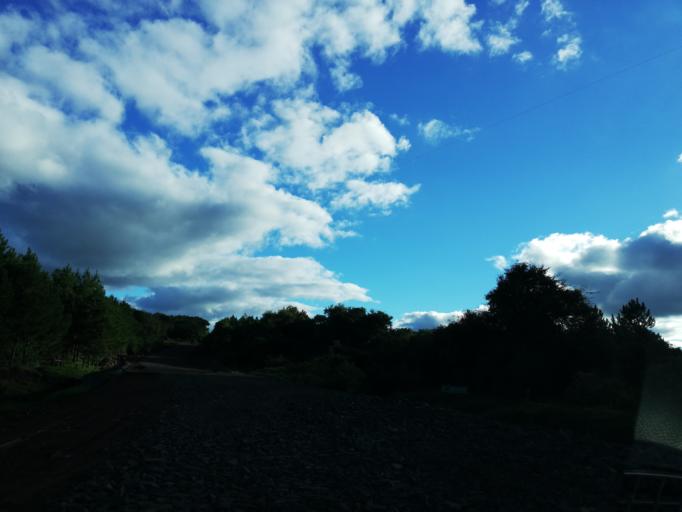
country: AR
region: Misiones
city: Almafuerte
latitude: -27.5526
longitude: -55.4193
